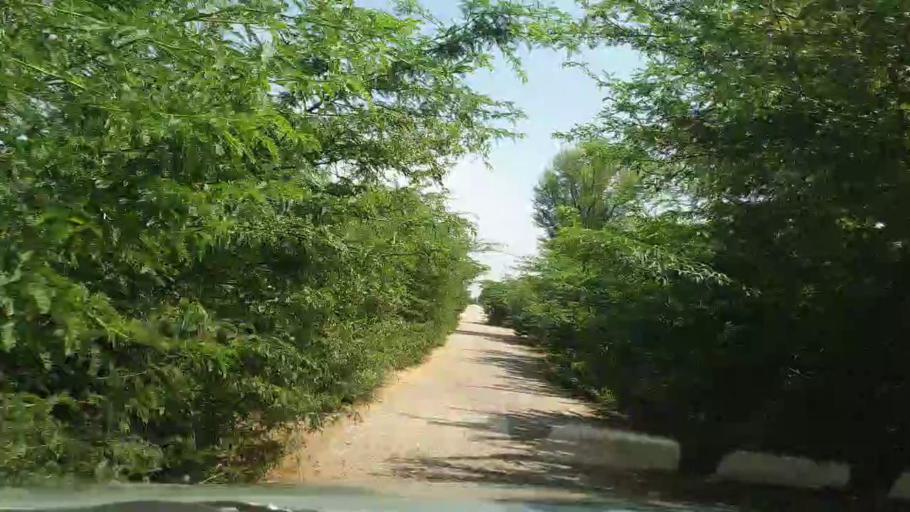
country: PK
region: Sindh
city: Bozdar
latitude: 27.0922
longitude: 68.9693
